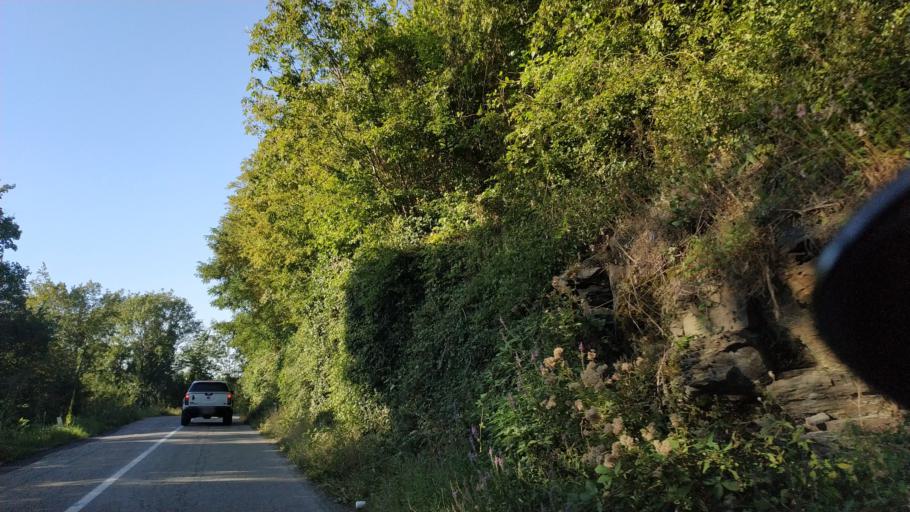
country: RS
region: Central Serbia
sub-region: Rasinski Okrug
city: Krusevac
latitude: 43.4635
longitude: 21.3599
